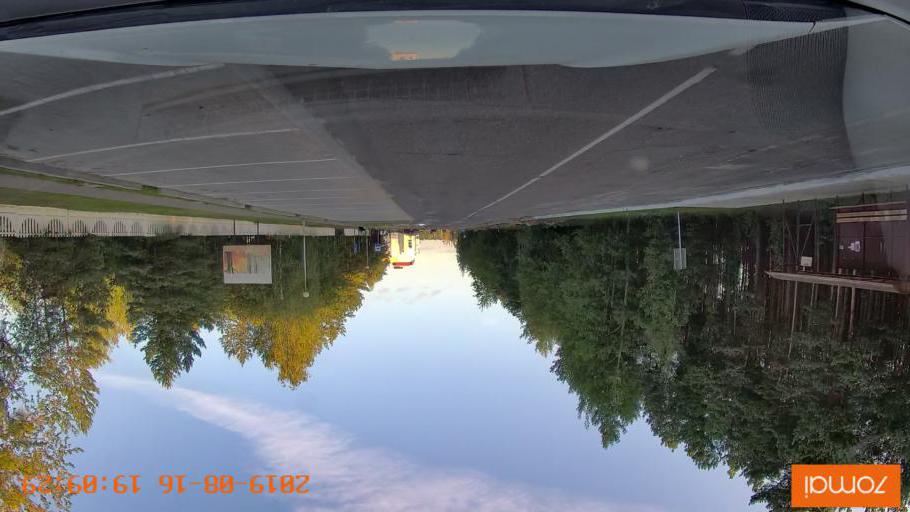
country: BY
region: Mogilev
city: Asipovichy
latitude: 53.3183
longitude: 28.6347
